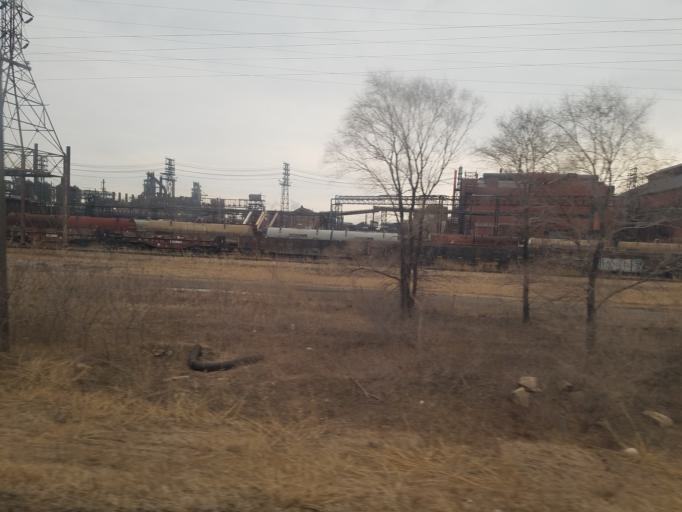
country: US
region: Indiana
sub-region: Lake County
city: East Chicago
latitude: 41.6567
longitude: -87.4474
